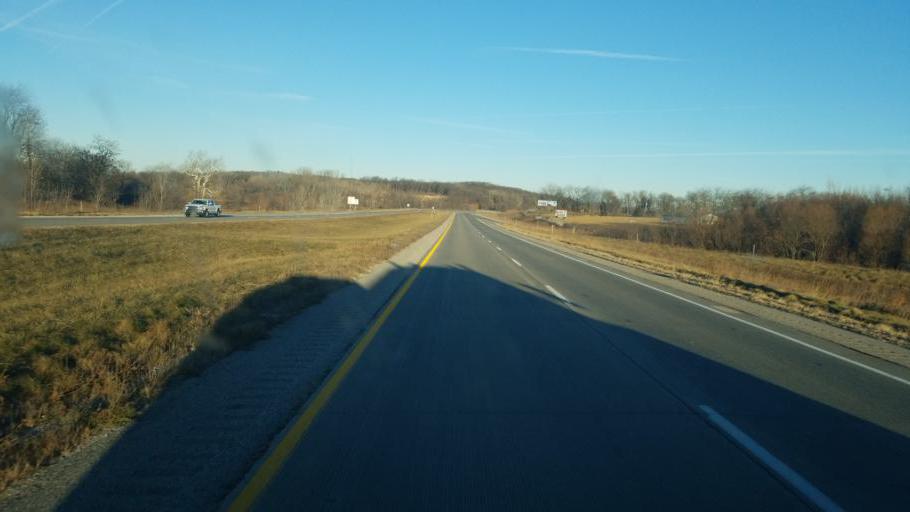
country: US
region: Iowa
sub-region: Wapello County
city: Eddyville
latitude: 41.1762
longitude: -92.6349
